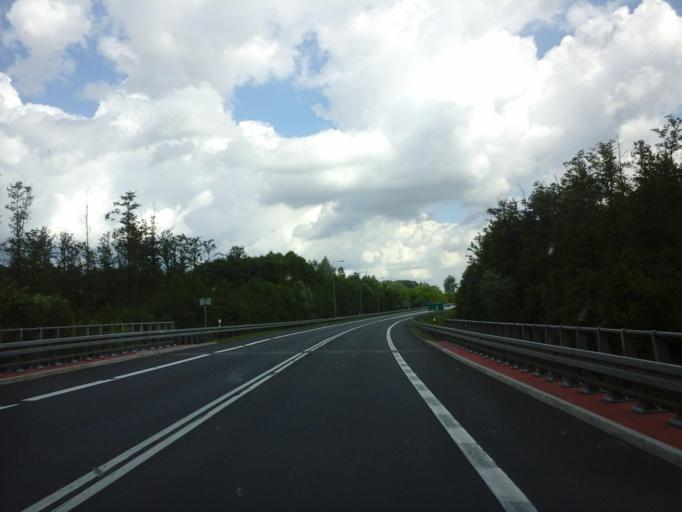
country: PL
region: West Pomeranian Voivodeship
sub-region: Powiat bialogardzki
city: Karlino
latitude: 54.0448
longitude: 15.8992
